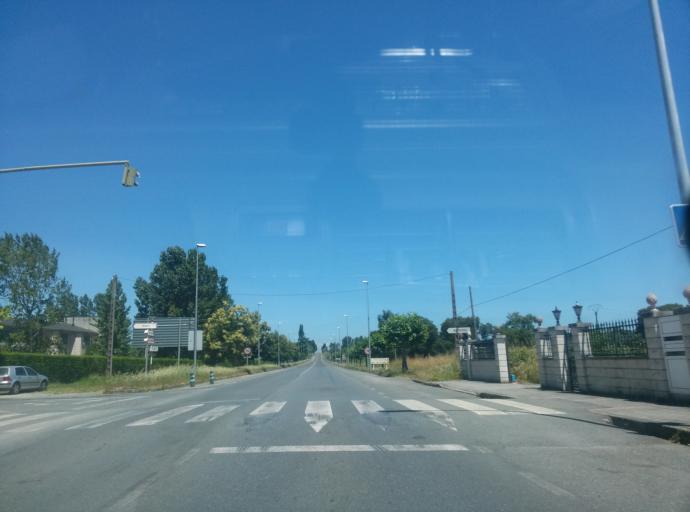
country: ES
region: Galicia
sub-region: Provincia de Lugo
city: Mos
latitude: 43.1489
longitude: -7.4897
